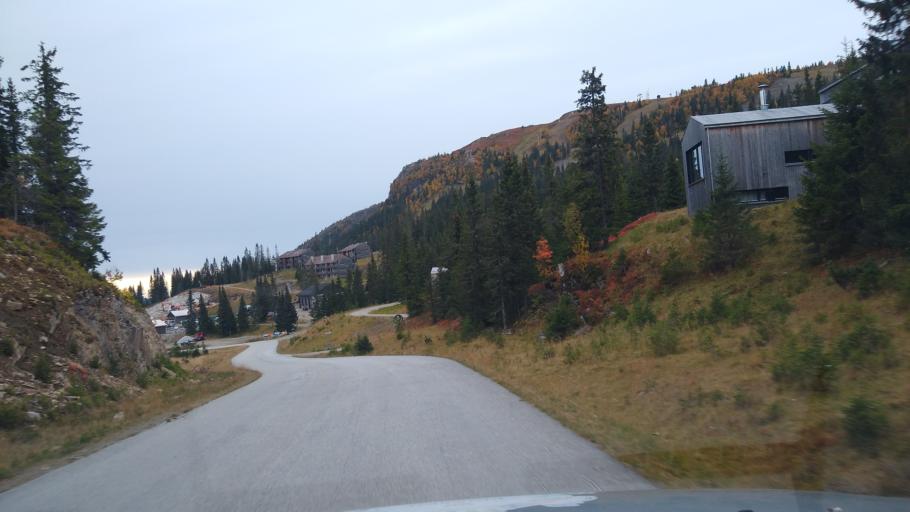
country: NO
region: Oppland
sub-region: Ringebu
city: Ringebu
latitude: 61.4755
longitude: 10.1284
